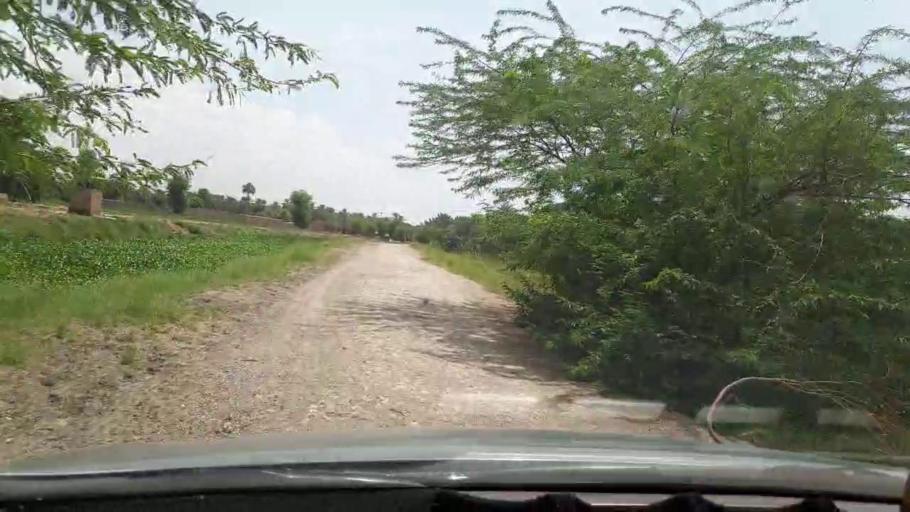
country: PK
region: Sindh
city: Khairpur
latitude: 27.4662
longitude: 68.7958
